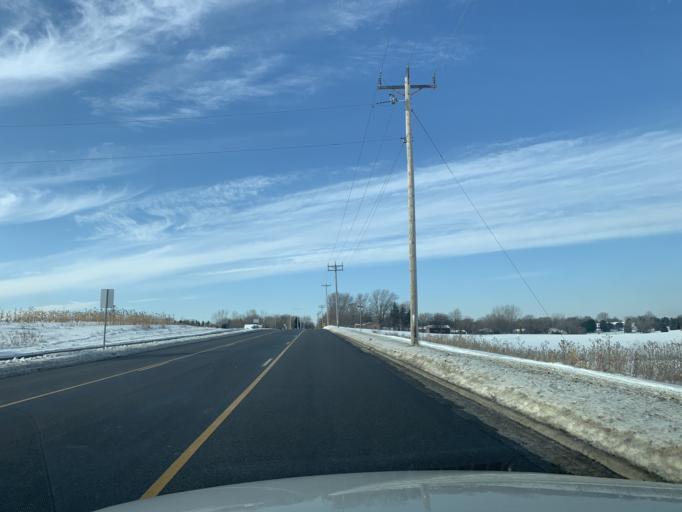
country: US
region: Minnesota
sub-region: Wright County
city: Albertville
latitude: 45.2243
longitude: -93.6395
